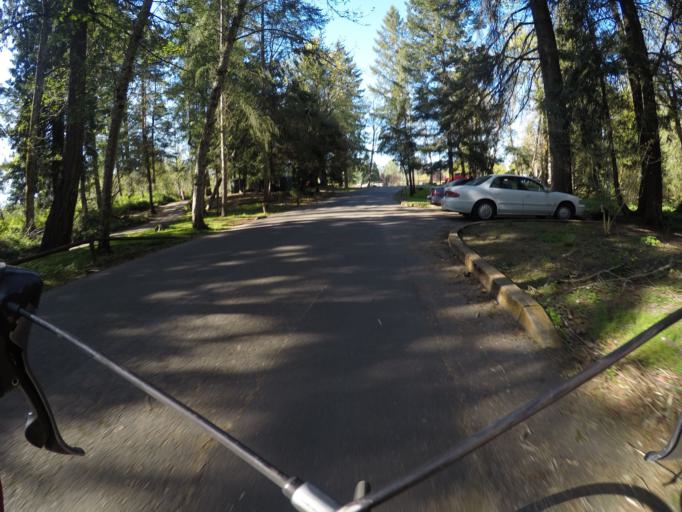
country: US
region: Oregon
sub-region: Washington County
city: Tualatin
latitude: 45.3947
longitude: -122.7736
